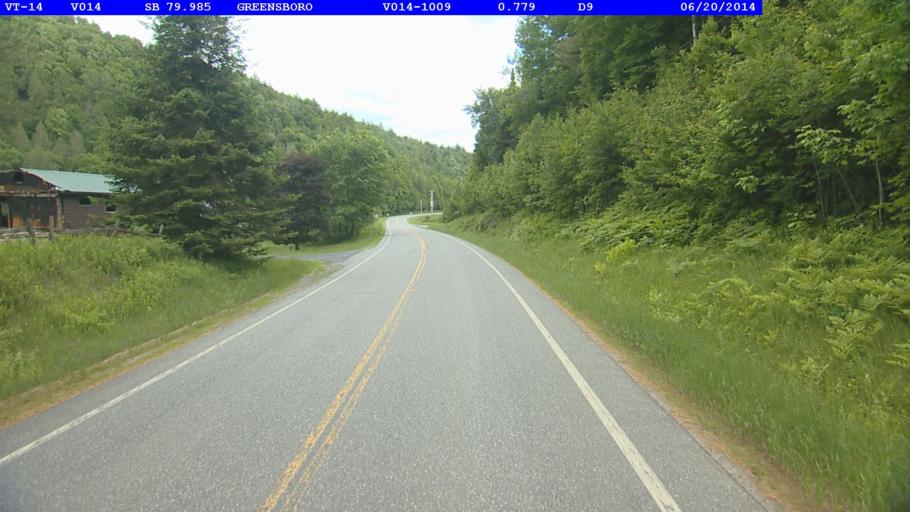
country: US
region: Vermont
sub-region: Caledonia County
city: Hardwick
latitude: 44.5904
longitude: -72.3592
